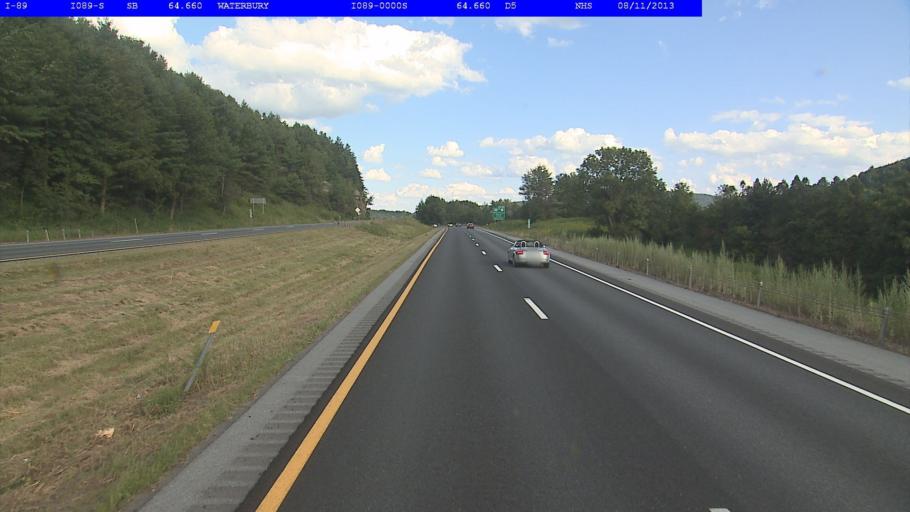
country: US
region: Vermont
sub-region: Washington County
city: Waterbury
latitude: 44.3475
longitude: -72.7688
